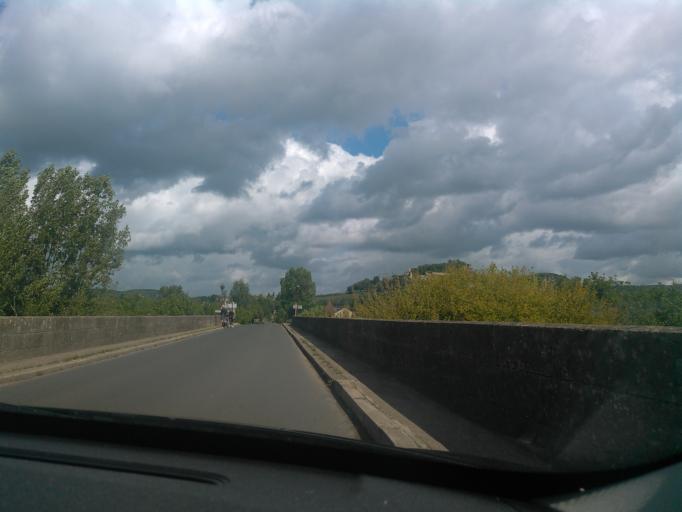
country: FR
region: Aquitaine
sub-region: Departement de la Dordogne
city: Cenac-et-Saint-Julien
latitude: 44.8151
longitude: 1.1524
